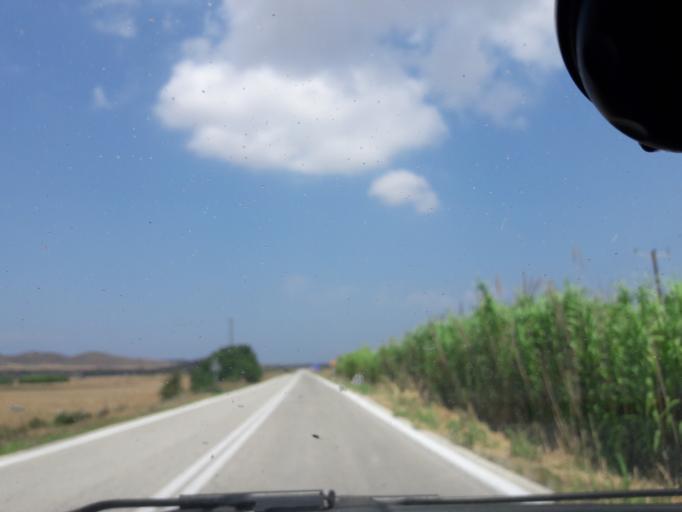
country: GR
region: North Aegean
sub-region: Nomos Lesvou
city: Myrina
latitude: 39.9604
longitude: 25.3677
